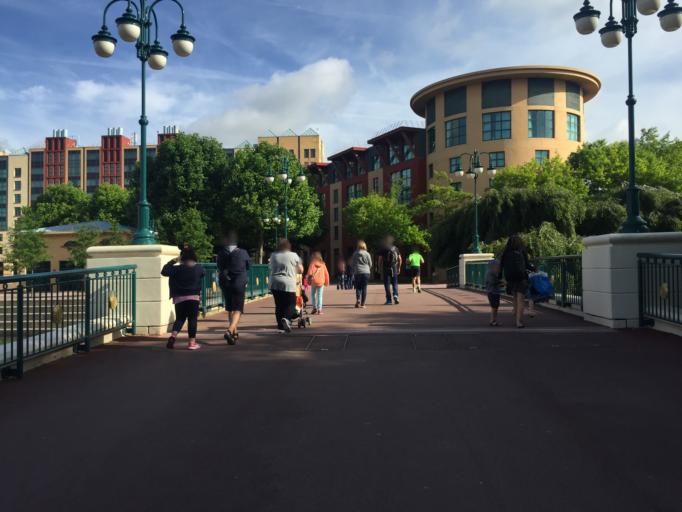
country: FR
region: Ile-de-France
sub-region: Departement de Seine-et-Marne
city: Serris
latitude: 48.8694
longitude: 2.7889
